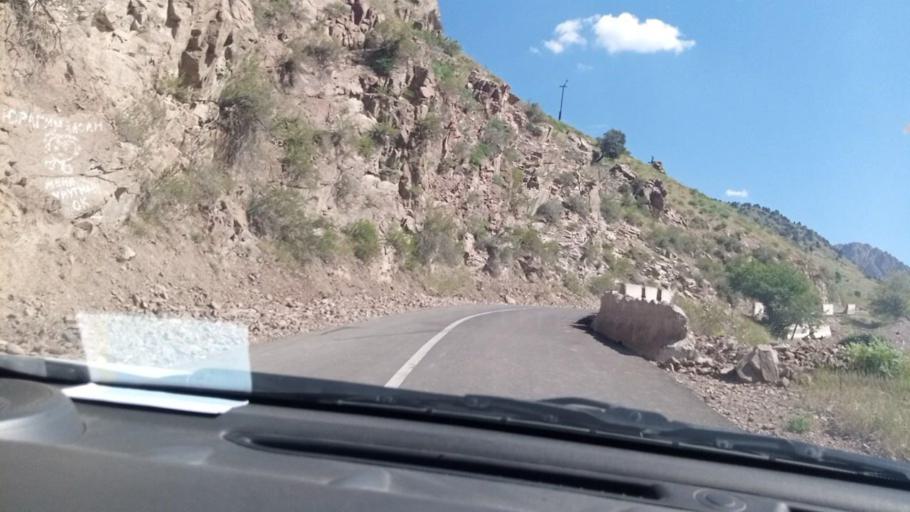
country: UZ
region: Toshkent
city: Yangiobod
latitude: 41.1259
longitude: 70.1074
